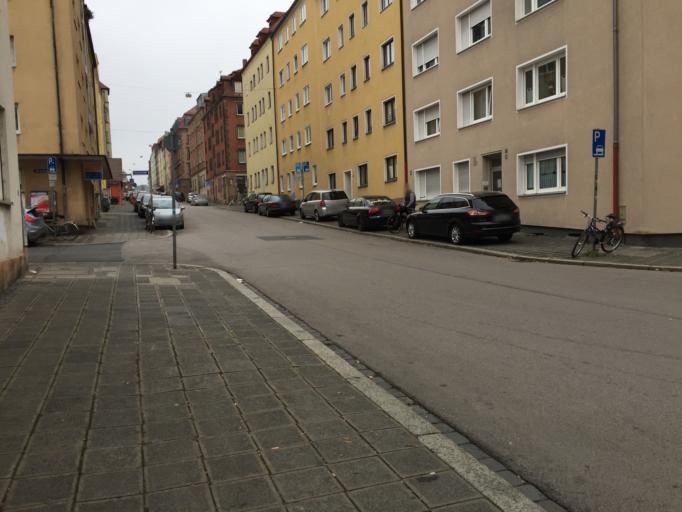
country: DE
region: Bavaria
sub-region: Regierungsbezirk Mittelfranken
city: Wetzendorf
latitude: 49.4574
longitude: 11.0564
